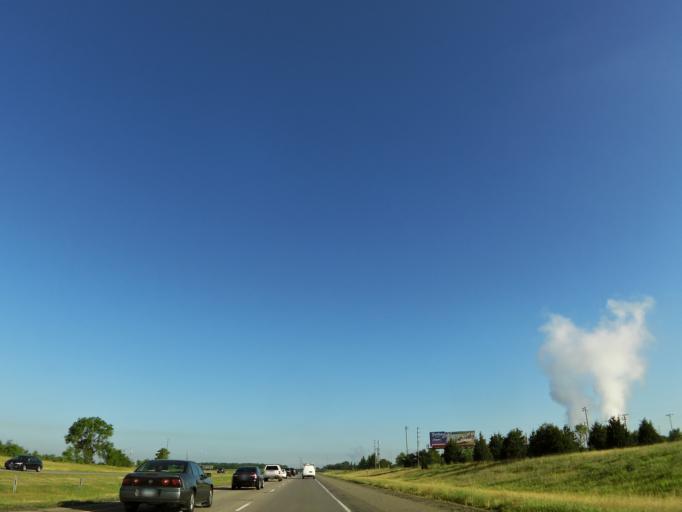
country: US
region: Minnesota
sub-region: Wright County
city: Monticello
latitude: 45.3206
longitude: -93.8408
